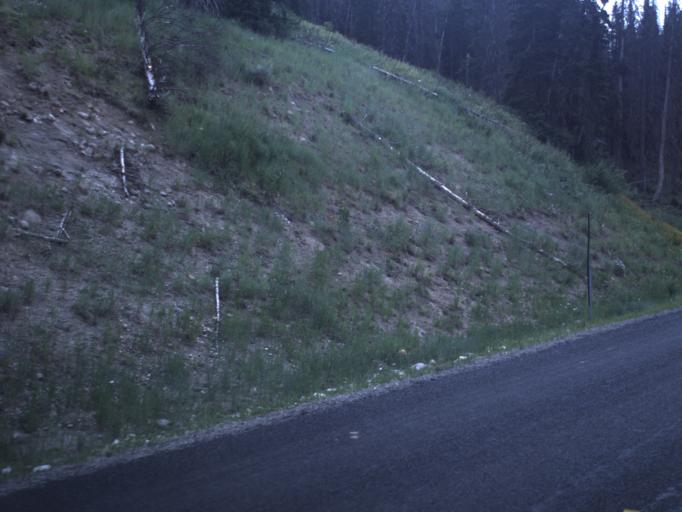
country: US
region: Utah
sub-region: Summit County
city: Francis
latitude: 40.4908
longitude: -111.0343
